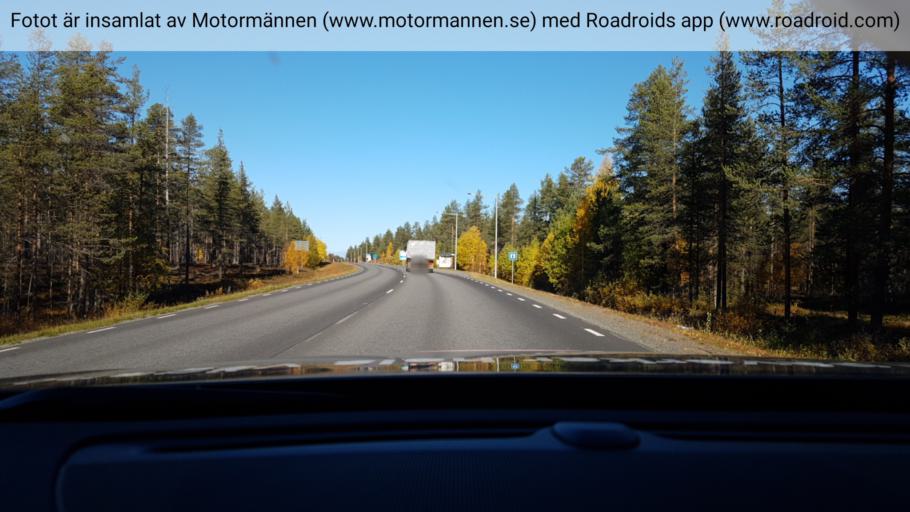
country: SE
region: Norrbotten
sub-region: Arvidsjaurs Kommun
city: Arvidsjaur
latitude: 65.5769
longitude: 19.2170
